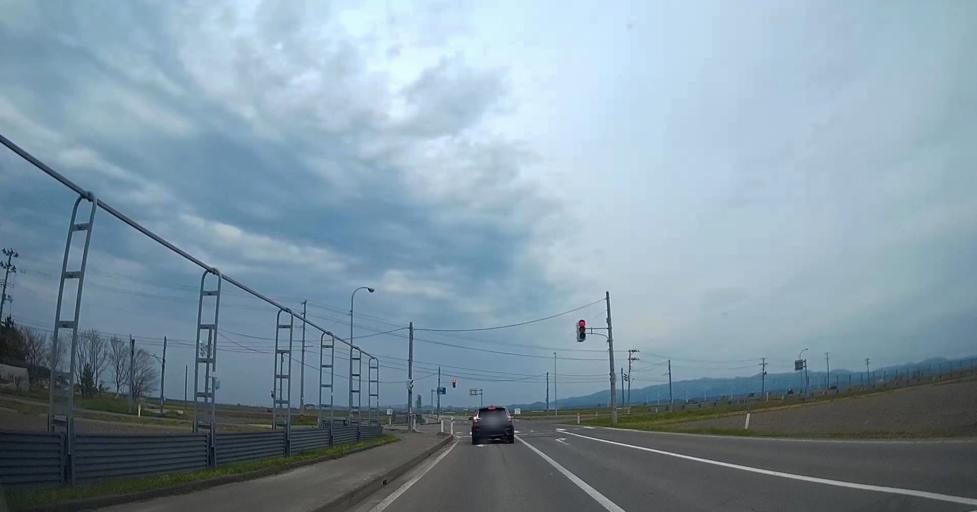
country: JP
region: Aomori
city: Shimokizukuri
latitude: 40.9845
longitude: 140.3762
